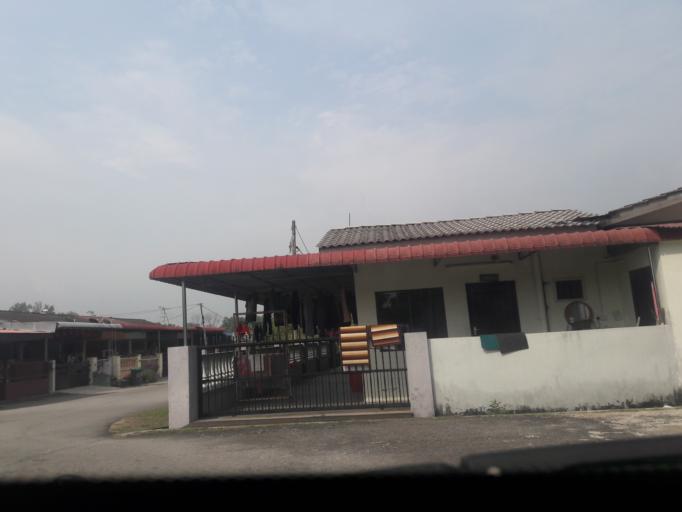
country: MY
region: Kedah
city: Kulim
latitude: 5.3587
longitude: 100.5418
